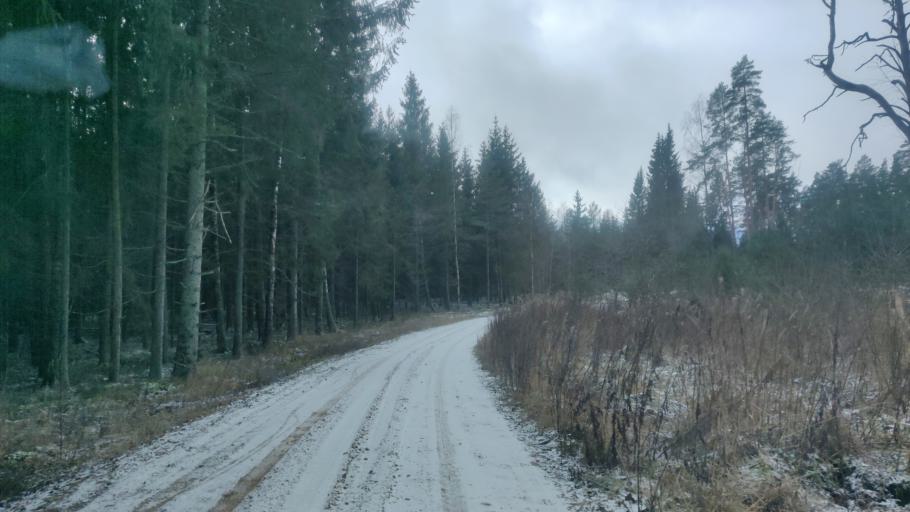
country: LT
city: Trakai
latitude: 54.5726
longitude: 24.9405
